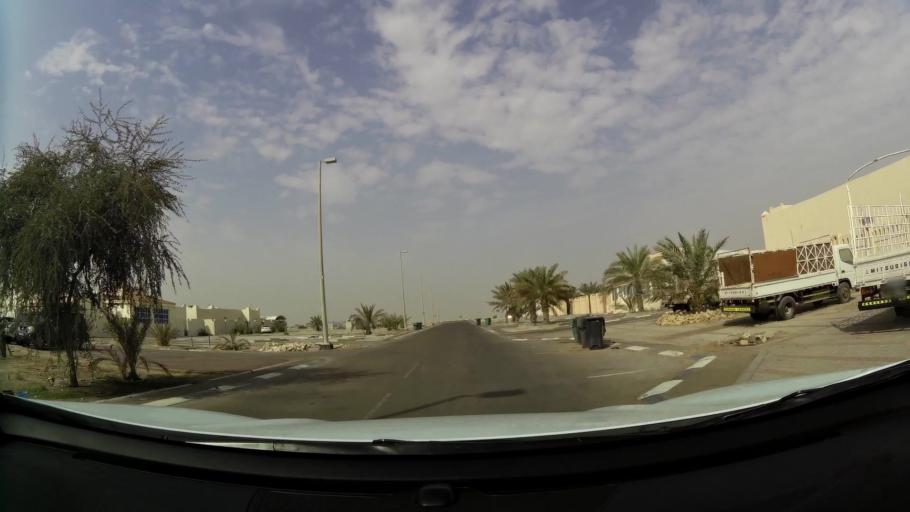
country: AE
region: Abu Dhabi
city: Abu Dhabi
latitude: 24.2790
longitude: 54.6859
